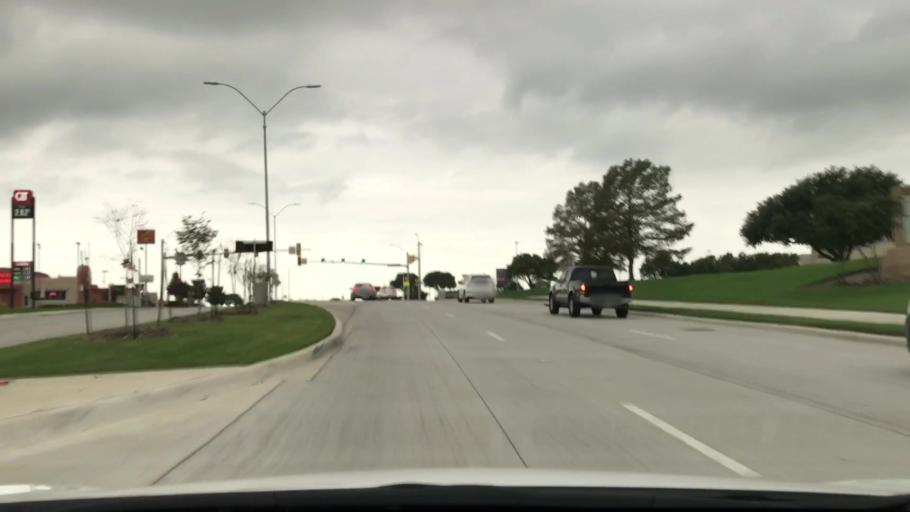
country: US
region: Texas
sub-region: Tarrant County
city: Watauga
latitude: 32.8449
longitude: -97.2905
